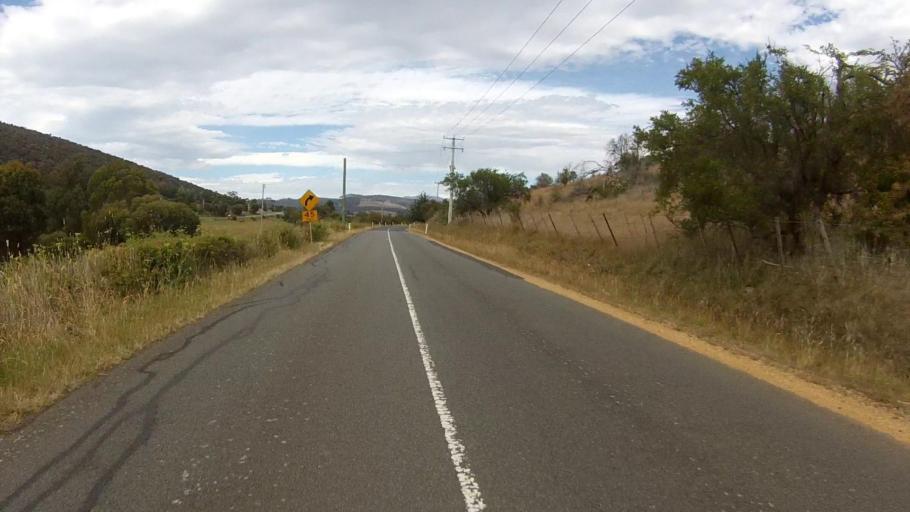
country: AU
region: Tasmania
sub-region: Clarence
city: Cambridge
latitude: -42.7390
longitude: 147.4227
